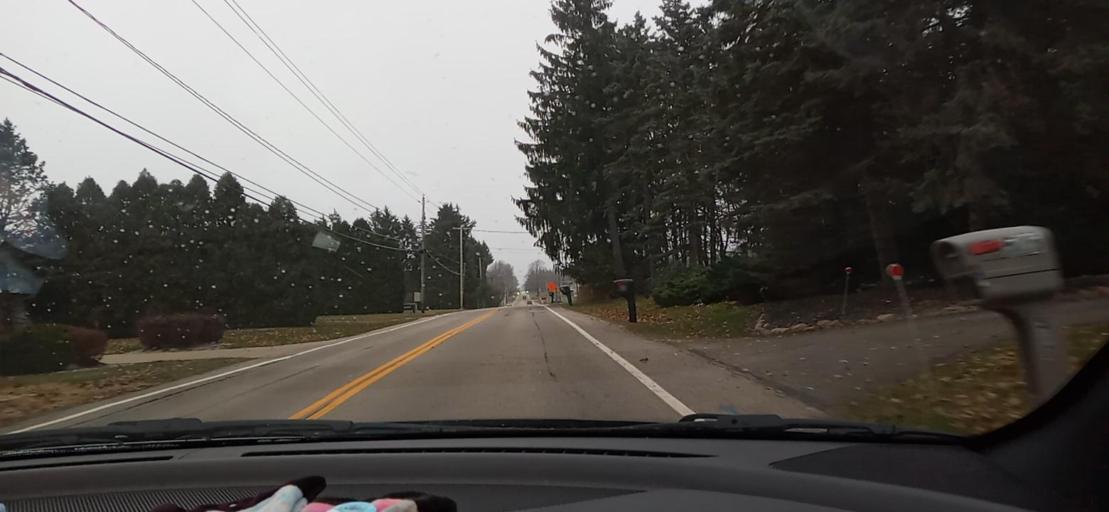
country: US
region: Ohio
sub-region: Summit County
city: Fairlawn
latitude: 41.1363
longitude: -81.5973
